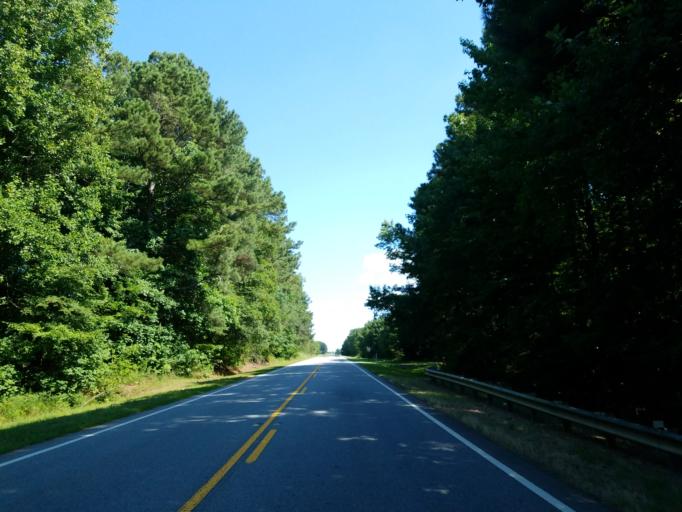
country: US
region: Georgia
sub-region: Crawford County
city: Roberta
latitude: 32.8174
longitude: -84.0541
